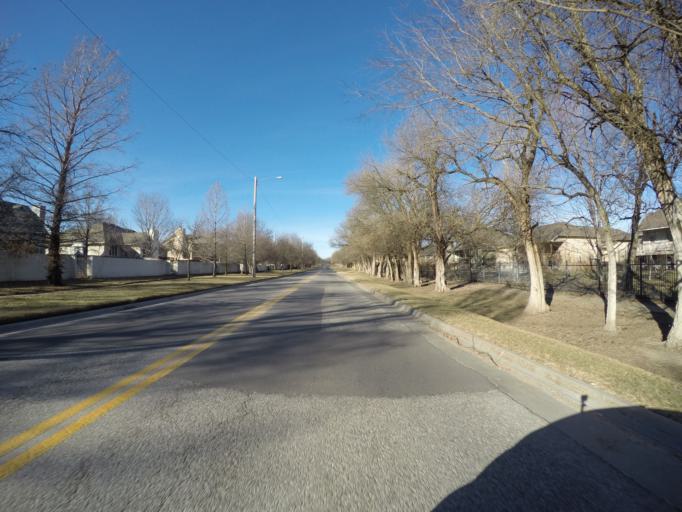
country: US
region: Kansas
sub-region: Sedgwick County
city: Maize
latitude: 37.7047
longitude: -97.4810
